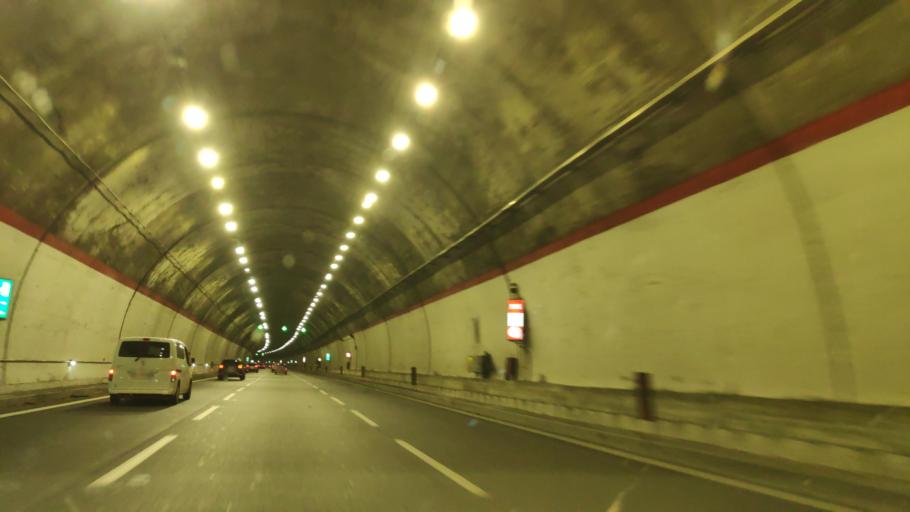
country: IT
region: Campania
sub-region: Provincia di Salerno
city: Contursi Terme
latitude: 40.6289
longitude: 15.2195
